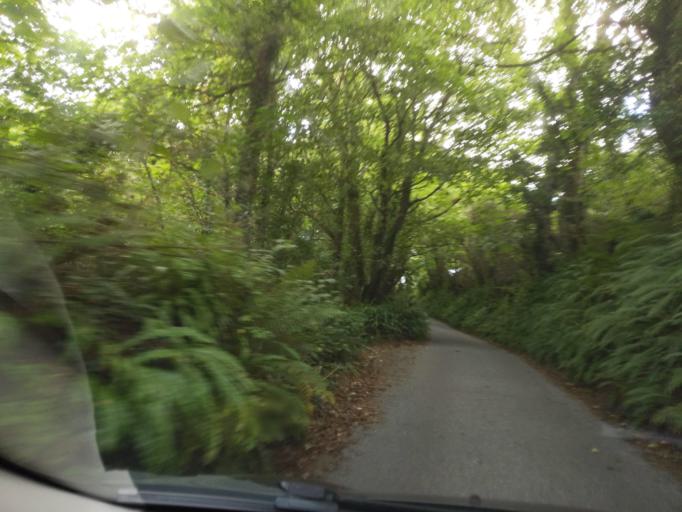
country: GB
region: England
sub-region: Plymouth
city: Plymstock
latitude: 50.3485
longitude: -4.1073
